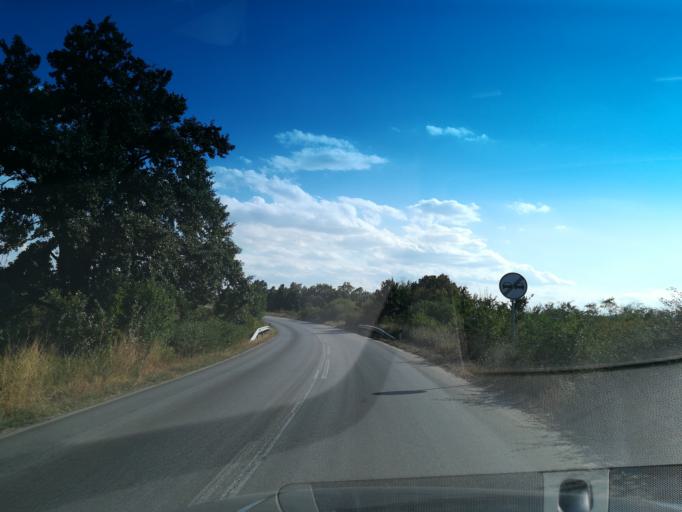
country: BG
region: Khaskovo
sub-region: Obshtina Mineralni Bani
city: Mineralni Bani
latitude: 41.9870
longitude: 25.3530
